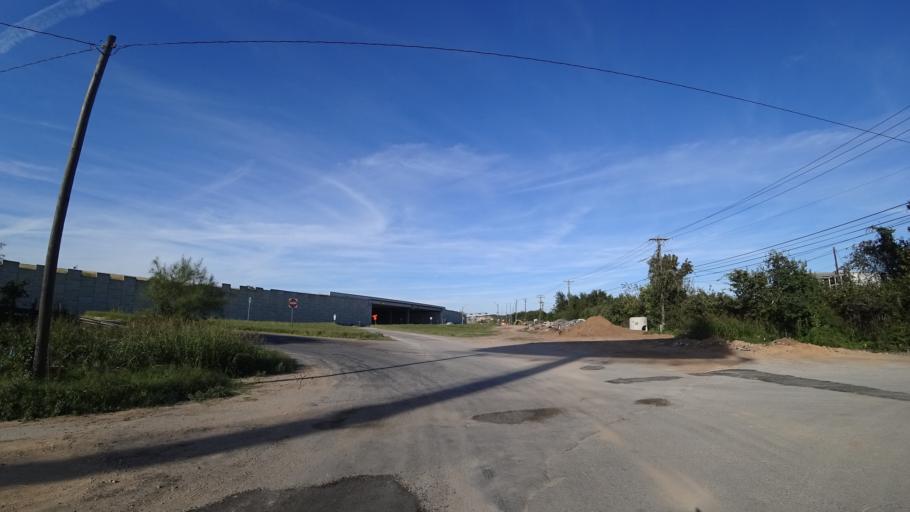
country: US
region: Texas
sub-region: Travis County
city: Austin
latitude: 30.2517
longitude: -97.6797
